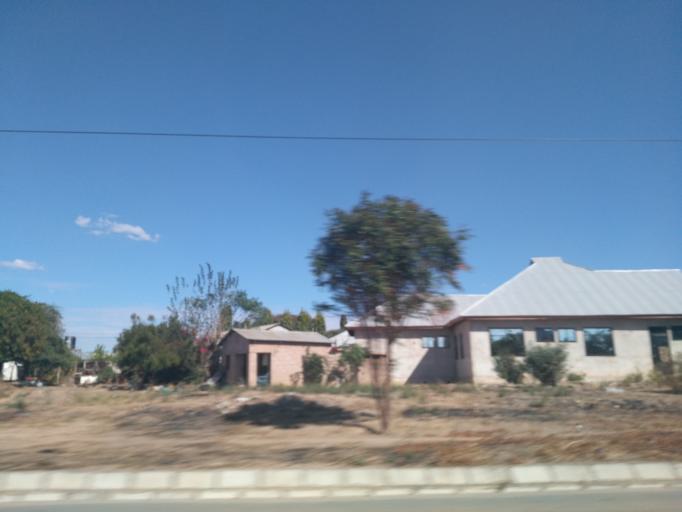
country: TZ
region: Dodoma
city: Dodoma
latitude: -6.1946
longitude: 35.7358
